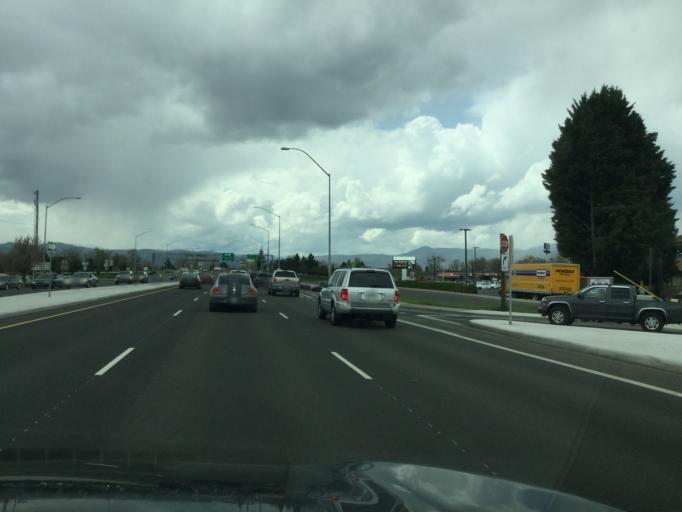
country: US
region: Oregon
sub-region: Jackson County
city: Medford
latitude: 42.3533
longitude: -122.8717
